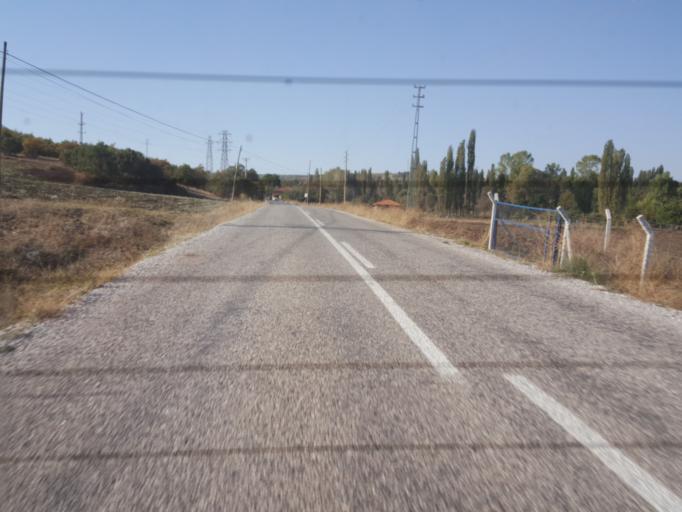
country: TR
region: Corum
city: Seydim
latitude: 40.5520
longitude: 34.7547
